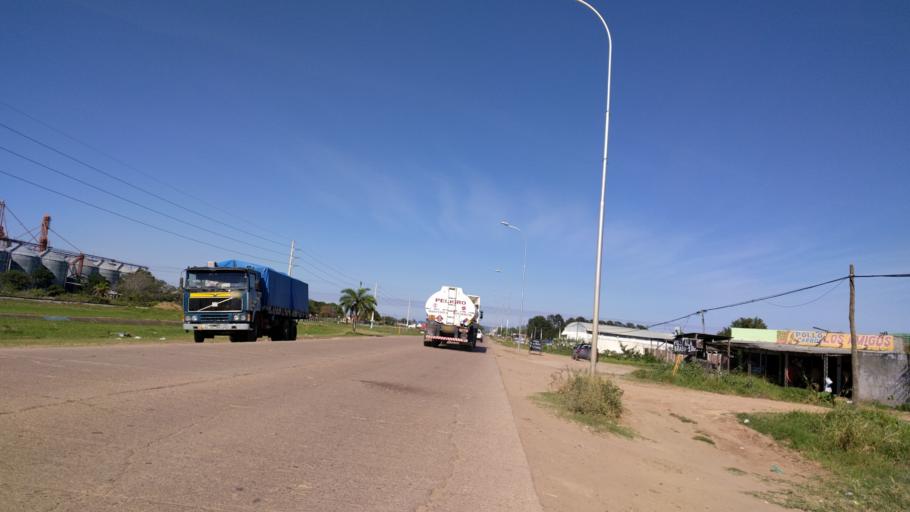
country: BO
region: Santa Cruz
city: Santa Cruz de la Sierra
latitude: -17.8676
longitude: -63.1911
